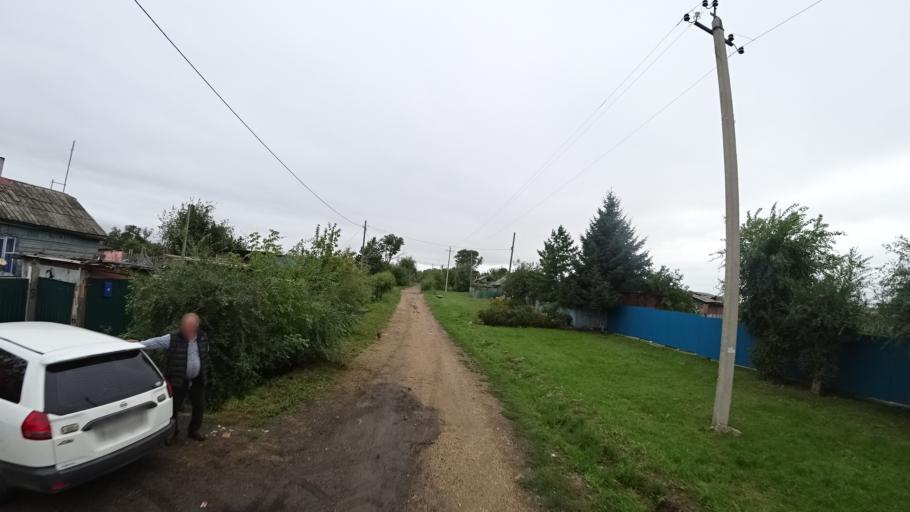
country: RU
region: Primorskiy
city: Chernigovka
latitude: 44.3456
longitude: 132.5337
